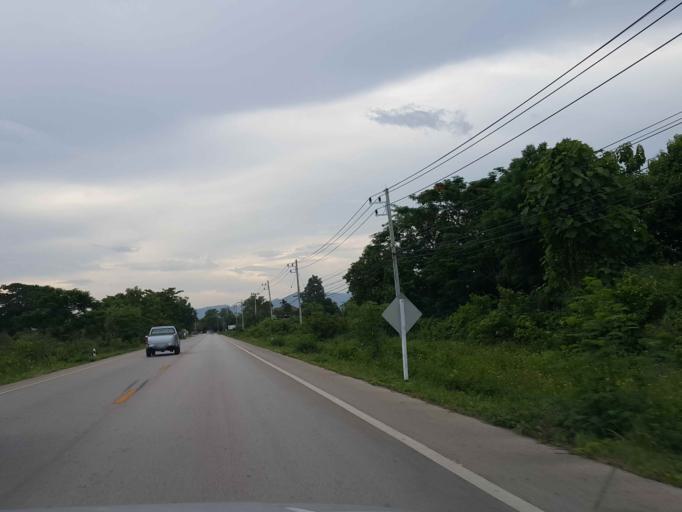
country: TH
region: Lampang
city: Hang Chat
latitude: 18.3011
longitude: 99.3709
